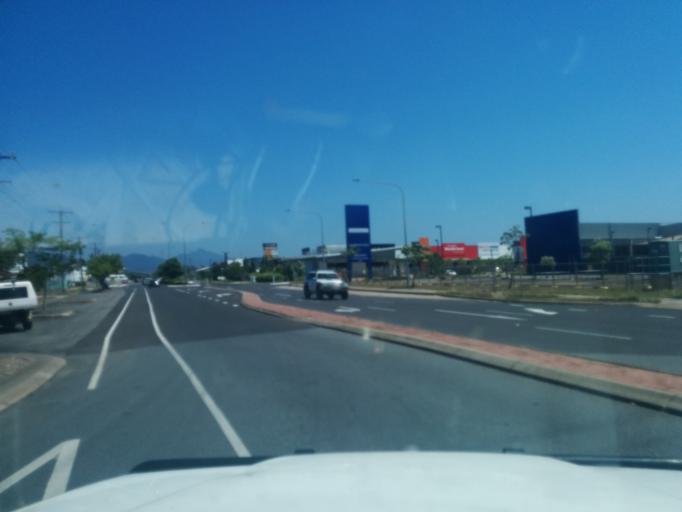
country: AU
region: Queensland
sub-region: Cairns
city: Cairns
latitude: -16.9310
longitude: 145.7724
